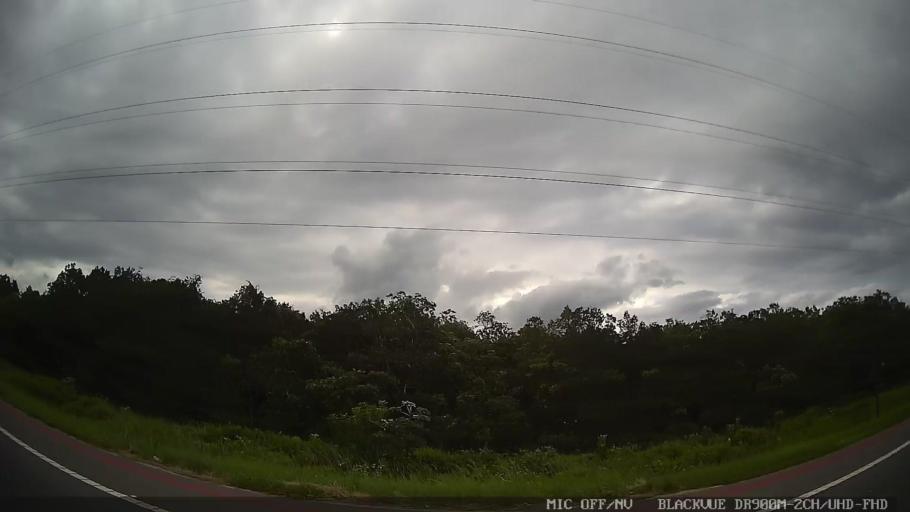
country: BR
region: Sao Paulo
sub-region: Itanhaem
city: Itanhaem
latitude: -24.1801
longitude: -46.8078
